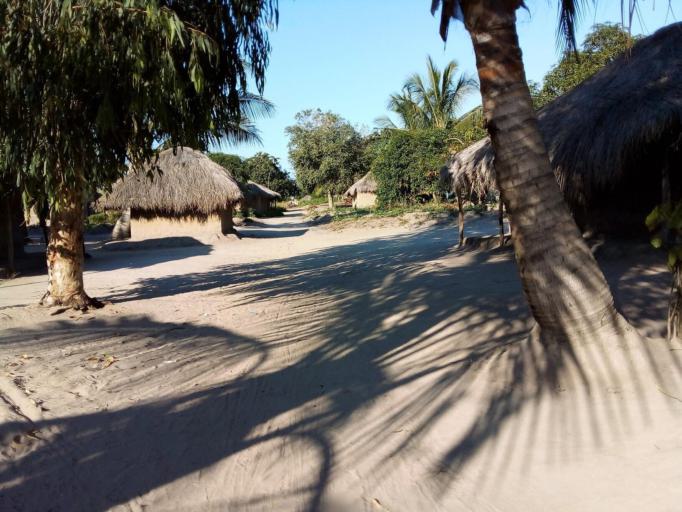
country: MZ
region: Zambezia
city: Quelimane
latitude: -17.5588
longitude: 36.6977
